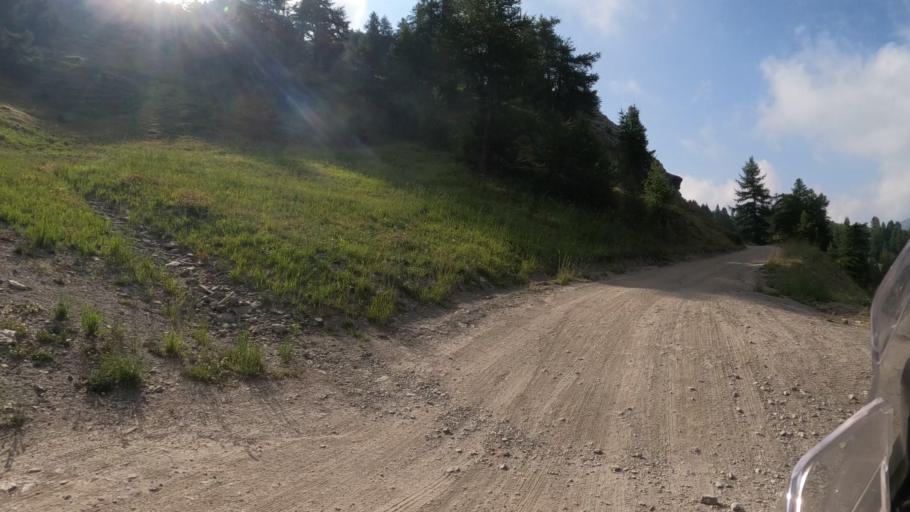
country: IT
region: Piedmont
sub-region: Provincia di Torino
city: Sauze d'Oulx
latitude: 45.0099
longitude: 6.8930
